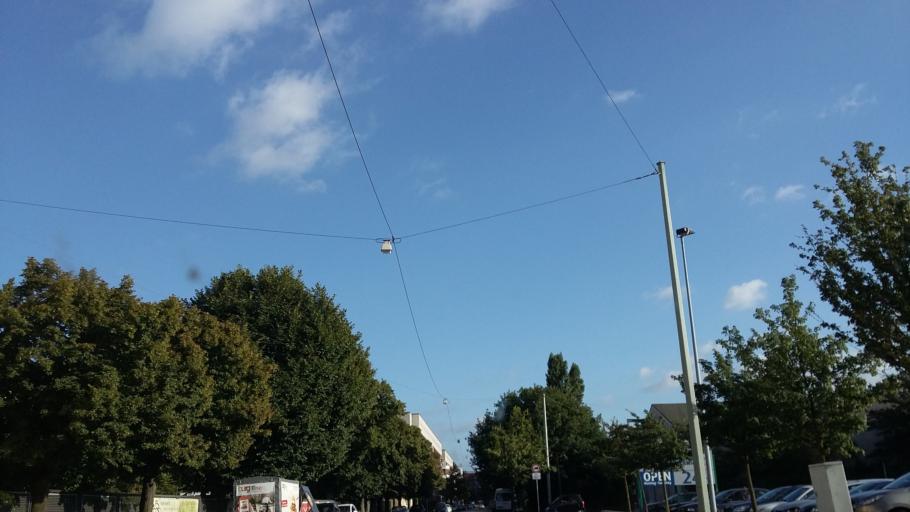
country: DE
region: Bremen
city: Bremerhaven
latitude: 53.5600
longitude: 8.5662
